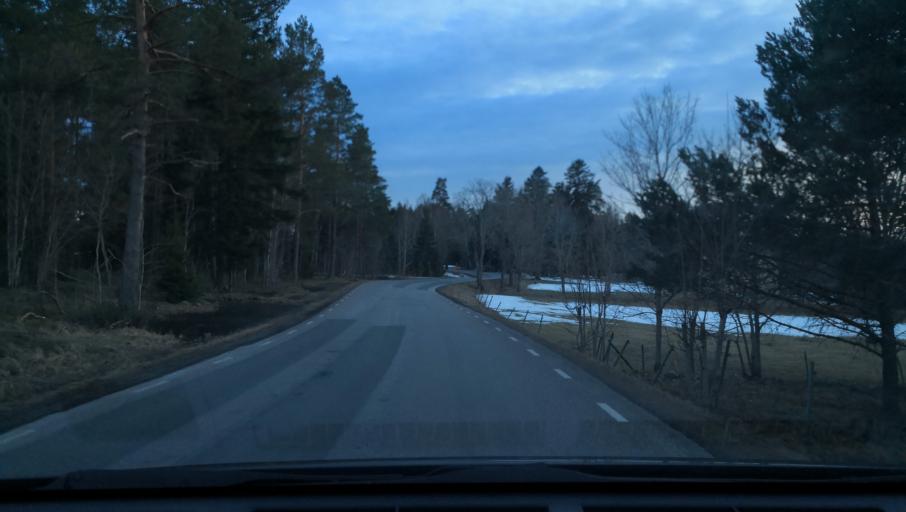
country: SE
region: Uppsala
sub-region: Osthammars Kommun
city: Osterbybruk
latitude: 60.2555
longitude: 17.9468
